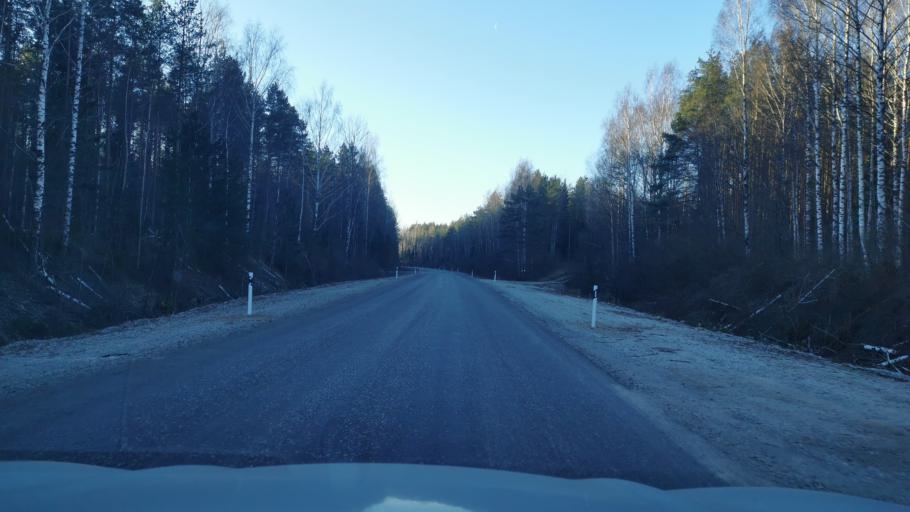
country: EE
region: Ida-Virumaa
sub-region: Kohtla-Nomme vald
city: Kohtla-Nomme
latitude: 59.3485
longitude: 27.1573
